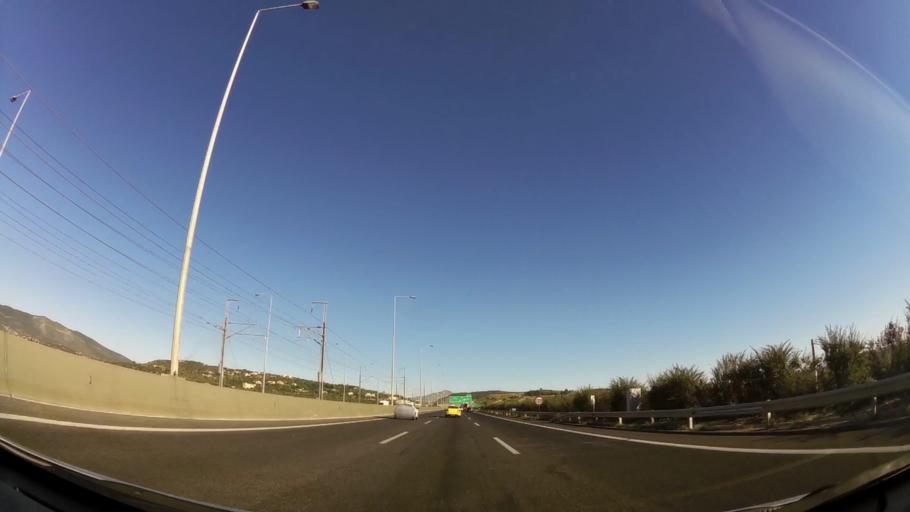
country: GR
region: Attica
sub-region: Nomarchia Anatolikis Attikis
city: Karellas
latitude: 37.9450
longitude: 23.8864
